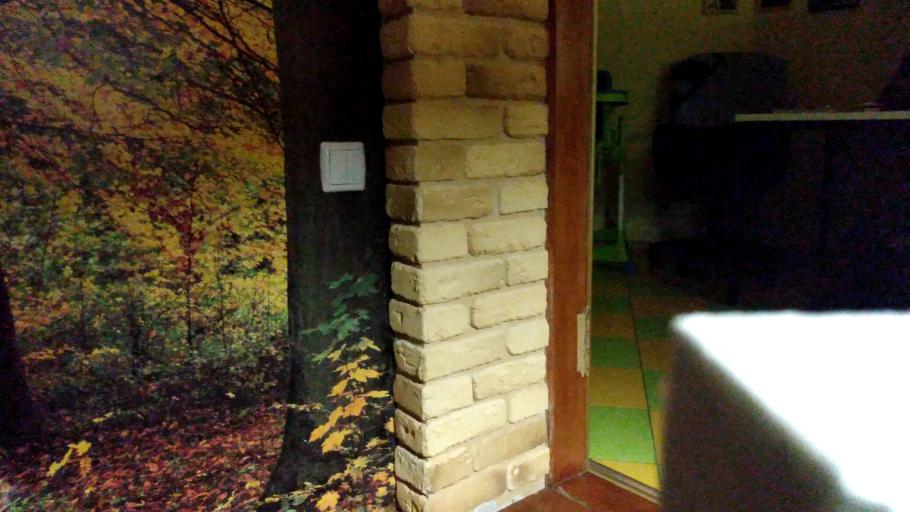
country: RU
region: Vologda
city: Lipin Bor
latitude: 60.8880
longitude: 38.0013
